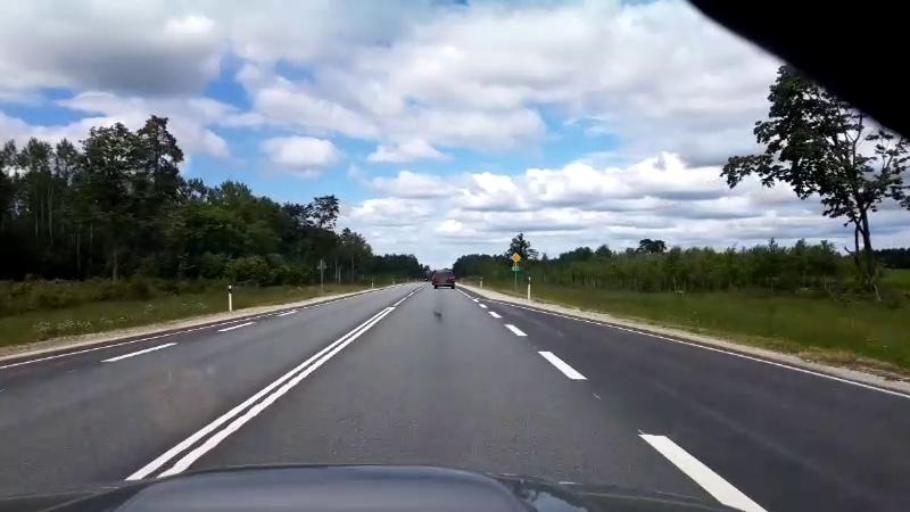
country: EE
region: Harju
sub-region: Nissi vald
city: Riisipere
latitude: 59.0652
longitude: 24.4500
